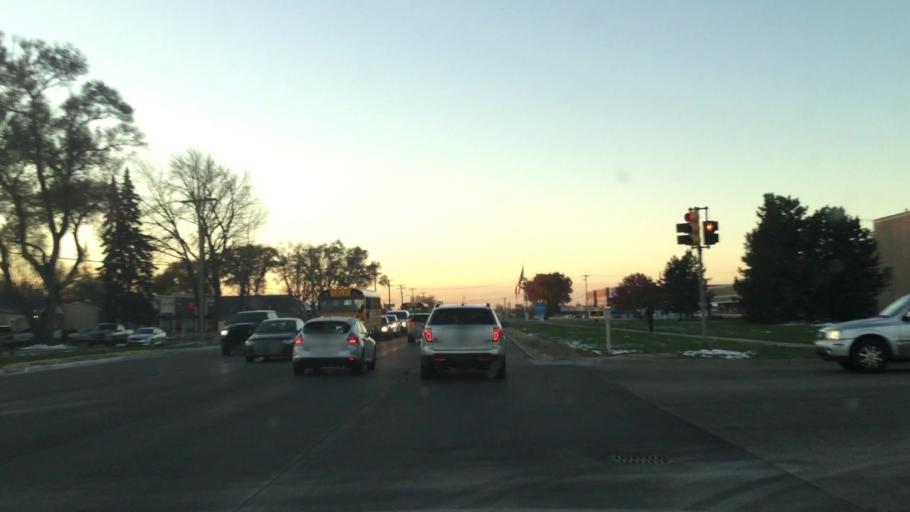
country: US
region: Michigan
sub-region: Macomb County
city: Utica
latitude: 42.6084
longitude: -83.0316
